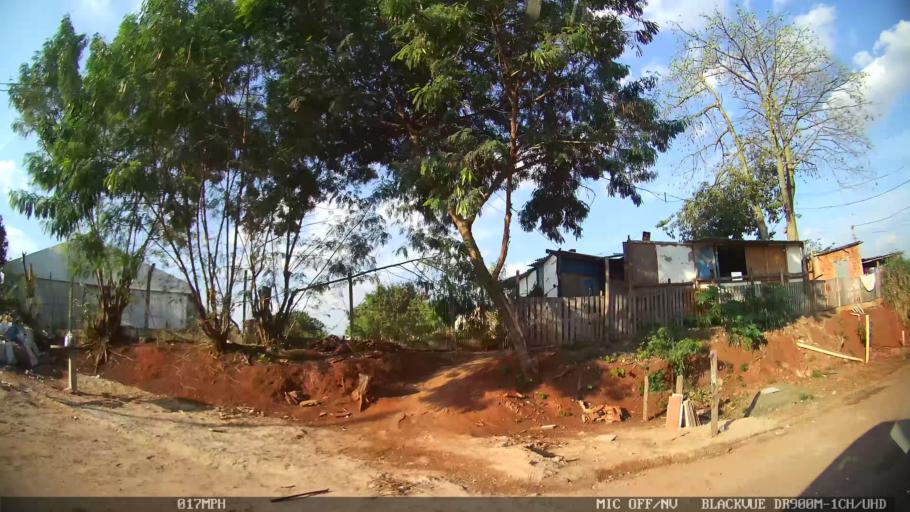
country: BR
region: Sao Paulo
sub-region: Hortolandia
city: Hortolandia
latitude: -22.8780
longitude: -47.1414
